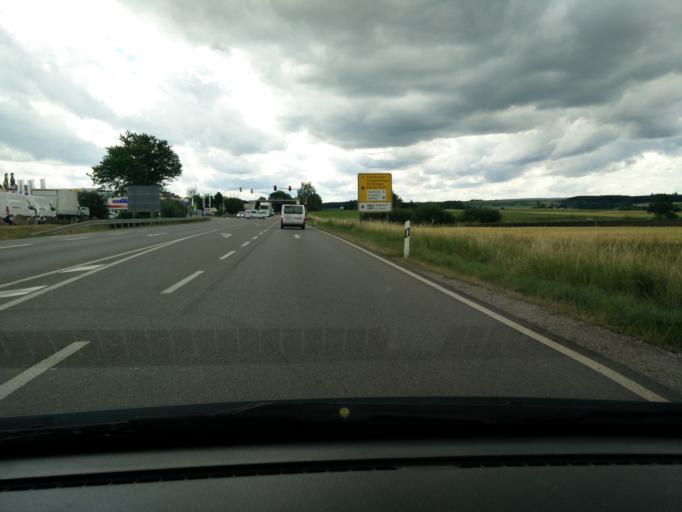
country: DE
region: Baden-Wuerttemberg
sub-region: Freiburg Region
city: Bad Durrheim
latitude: 48.0350
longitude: 8.5299
